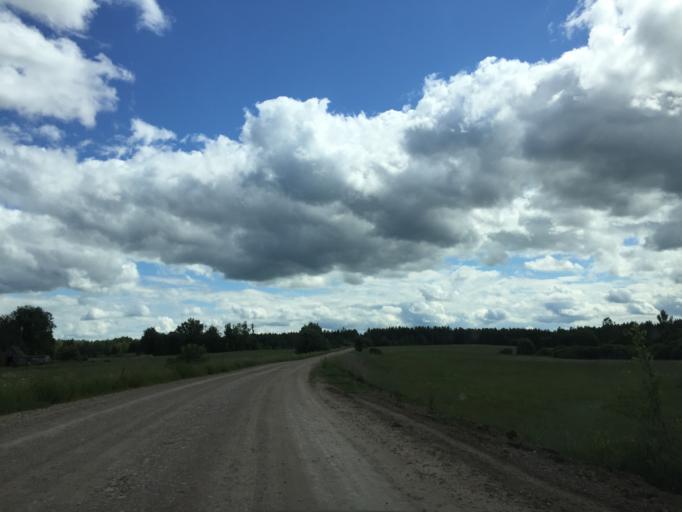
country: LV
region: Vecumnieki
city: Vecumnieki
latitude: 56.5023
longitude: 24.4061
